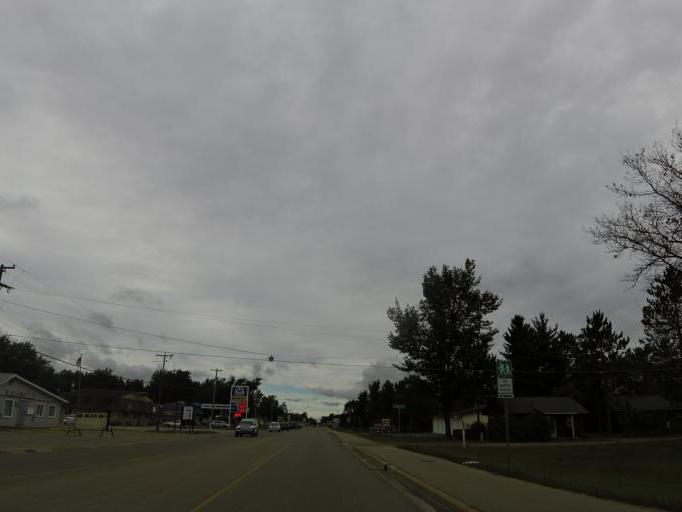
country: US
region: Michigan
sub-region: Roscommon County
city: Saint Helen
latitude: 44.3584
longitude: -84.4102
